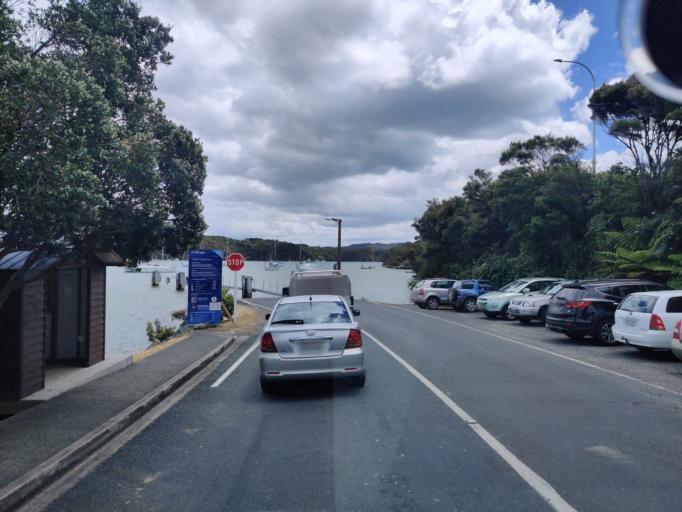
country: NZ
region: Northland
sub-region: Far North District
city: Paihia
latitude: -35.3051
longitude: 174.1194
